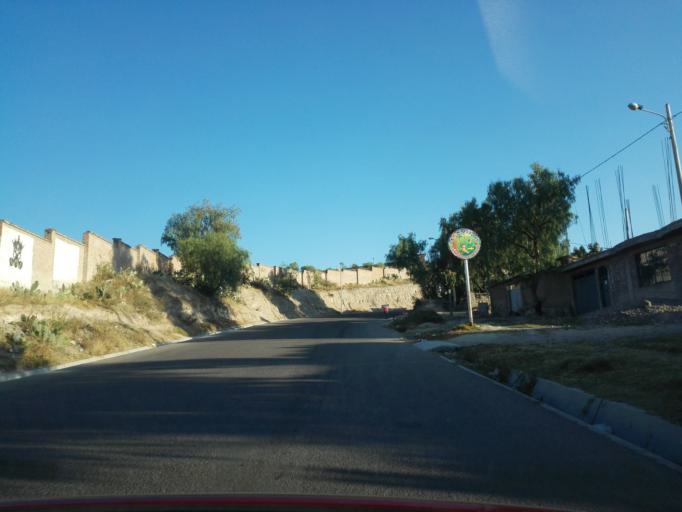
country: PE
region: Ayacucho
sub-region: Provincia de Huamanga
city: Ayacucho
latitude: -13.1414
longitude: -74.2224
